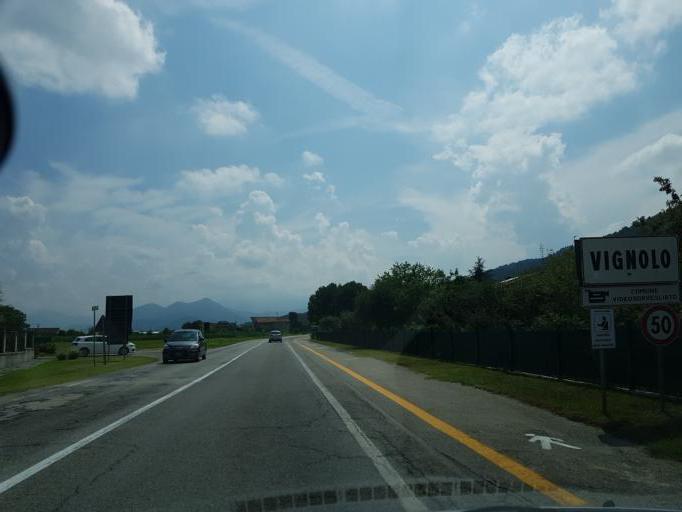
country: IT
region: Piedmont
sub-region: Provincia di Cuneo
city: Vignolo
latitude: 44.3699
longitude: 7.4745
